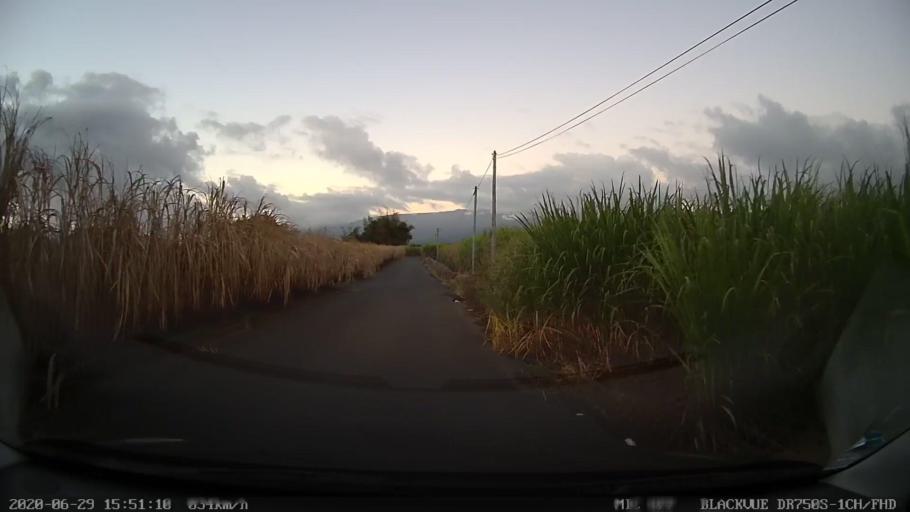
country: RE
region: Reunion
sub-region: Reunion
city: Bras-Panon
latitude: -20.9927
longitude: 55.6934
